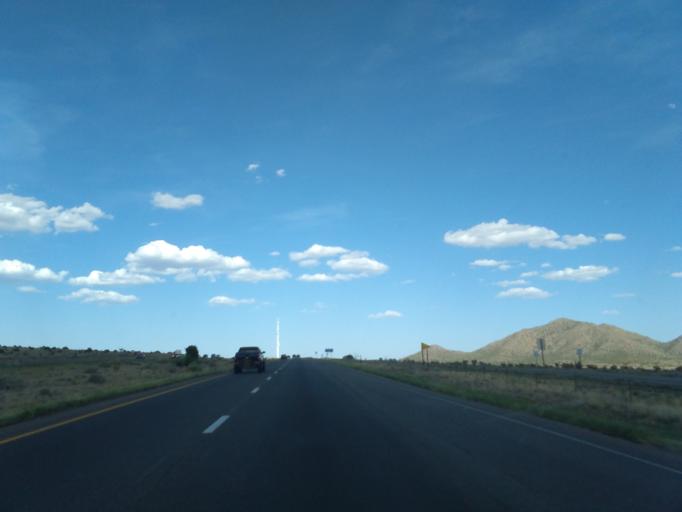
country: US
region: New Mexico
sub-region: Santa Fe County
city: La Cienega
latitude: 35.5209
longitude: -106.1762
